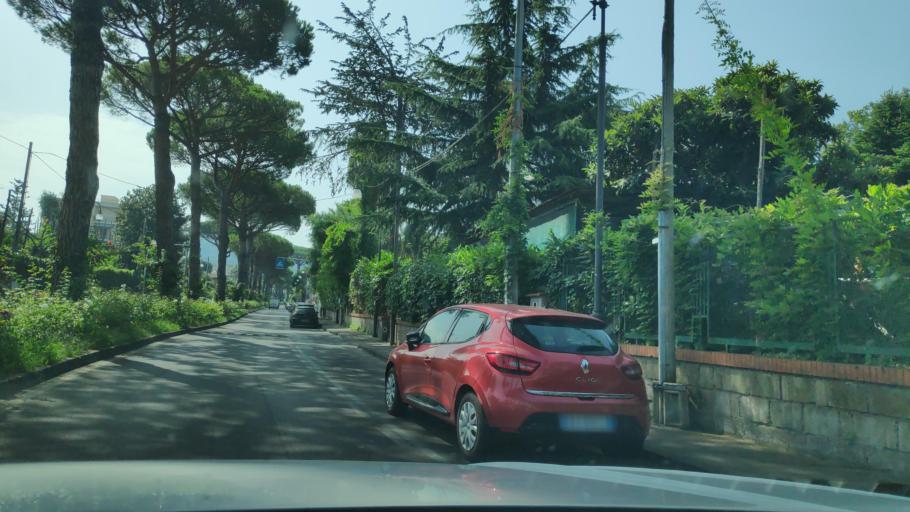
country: IT
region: Campania
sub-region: Provincia di Napoli
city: Sant'Agnello
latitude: 40.6353
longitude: 14.3948
